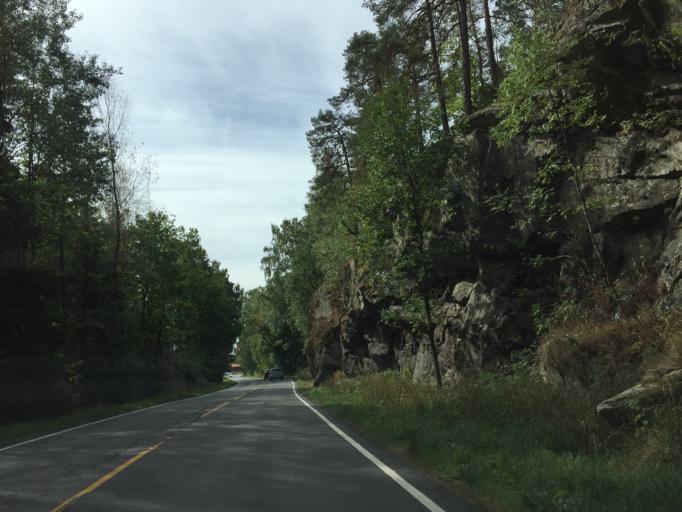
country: NO
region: Ostfold
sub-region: Moss
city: Moss
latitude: 59.4863
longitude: 10.6978
